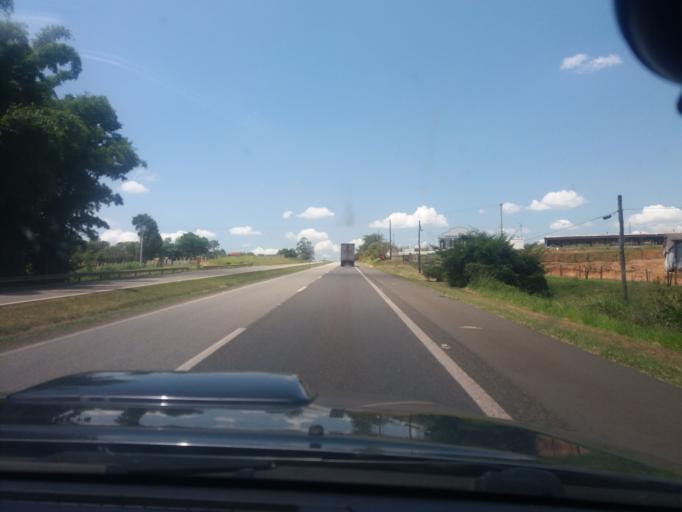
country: BR
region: Sao Paulo
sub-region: Tatui
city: Tatui
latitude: -23.4113
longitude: -47.9252
